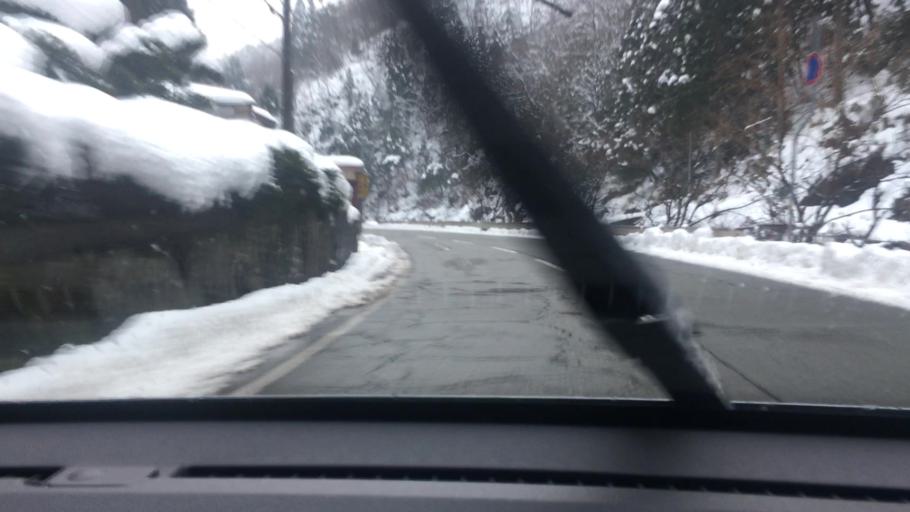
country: JP
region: Hyogo
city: Toyooka
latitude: 35.3708
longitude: 134.5769
